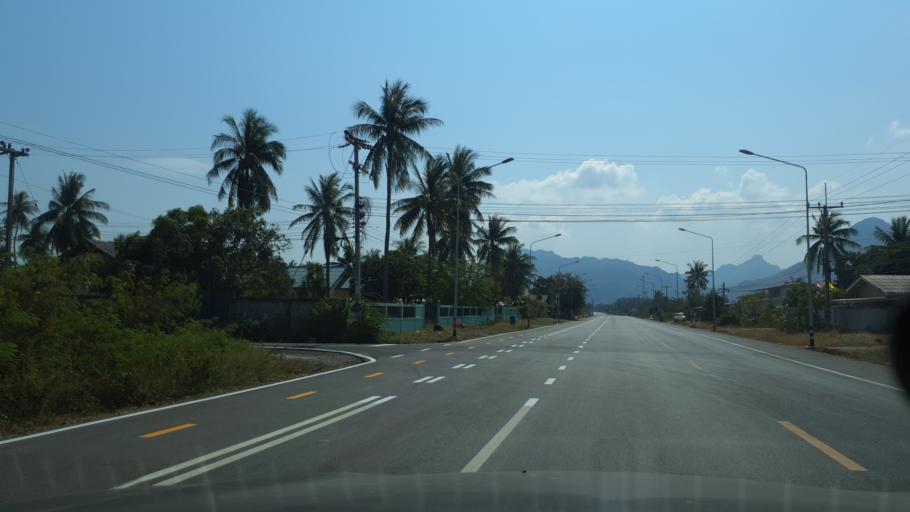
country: TH
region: Prachuap Khiri Khan
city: Sam Roi Yot
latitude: 12.2644
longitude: 99.9666
